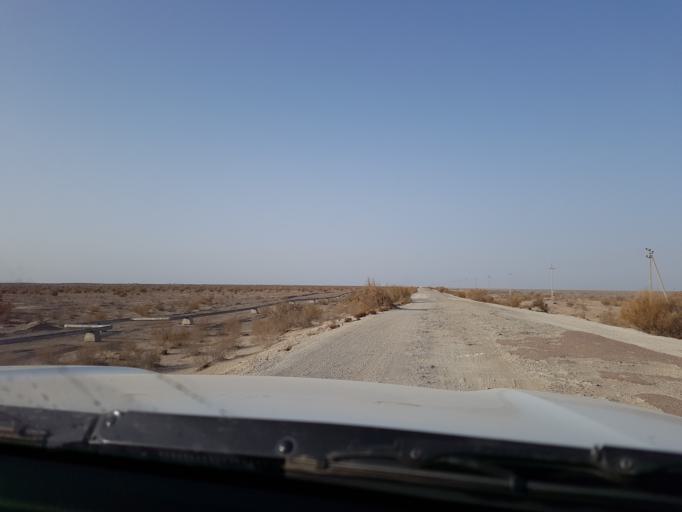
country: UZ
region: Karakalpakstan
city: Shumanay Shahri
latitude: 42.0029
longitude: 58.0681
